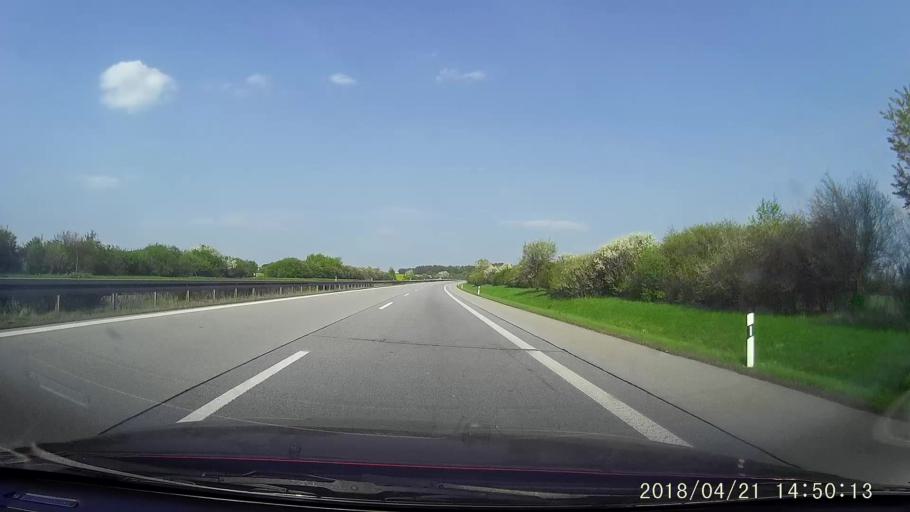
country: DE
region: Saxony
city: Kubschutz
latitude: 51.2046
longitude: 14.4858
